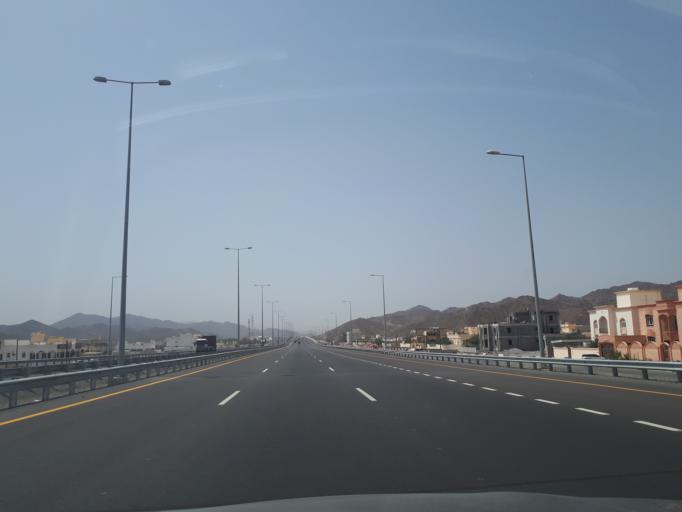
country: OM
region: Muhafazat ad Dakhiliyah
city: Bidbid
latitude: 23.3997
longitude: 58.0984
